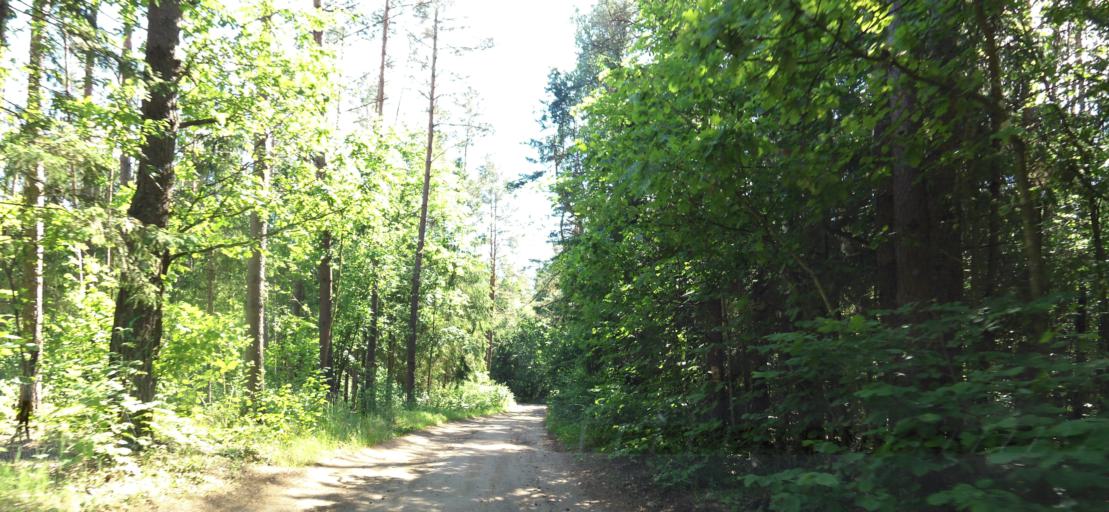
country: LT
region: Vilnius County
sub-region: Vilnius
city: Fabijoniskes
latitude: 54.8280
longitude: 25.3213
